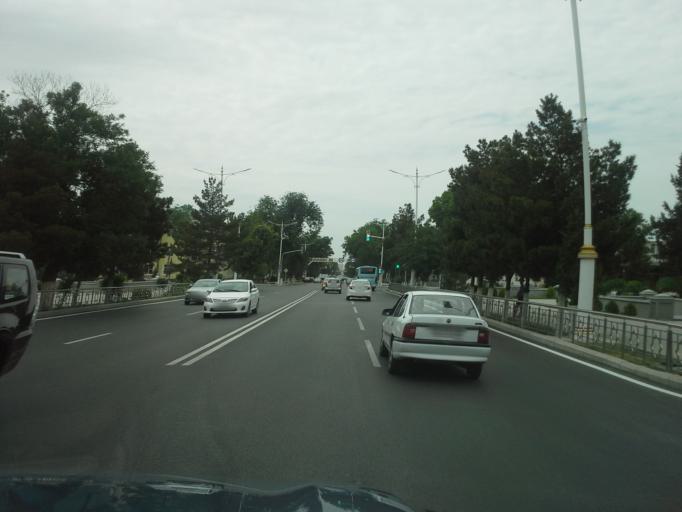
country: TM
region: Ahal
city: Ashgabat
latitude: 37.9468
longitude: 58.3794
